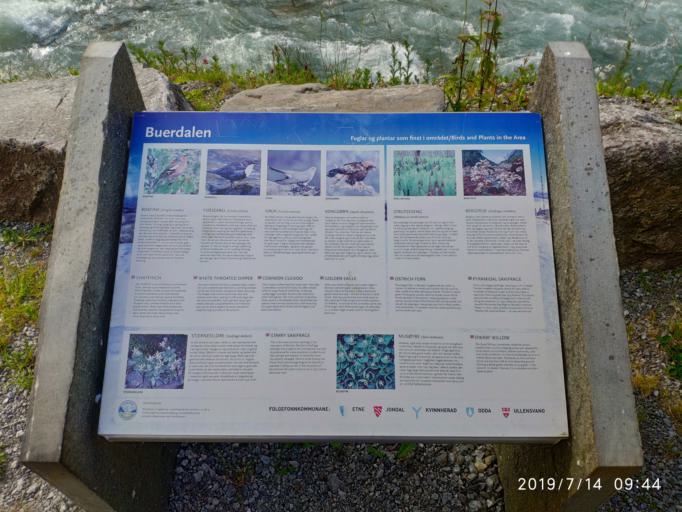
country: NO
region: Hordaland
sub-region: Odda
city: Odda
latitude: 60.0446
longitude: 6.4751
